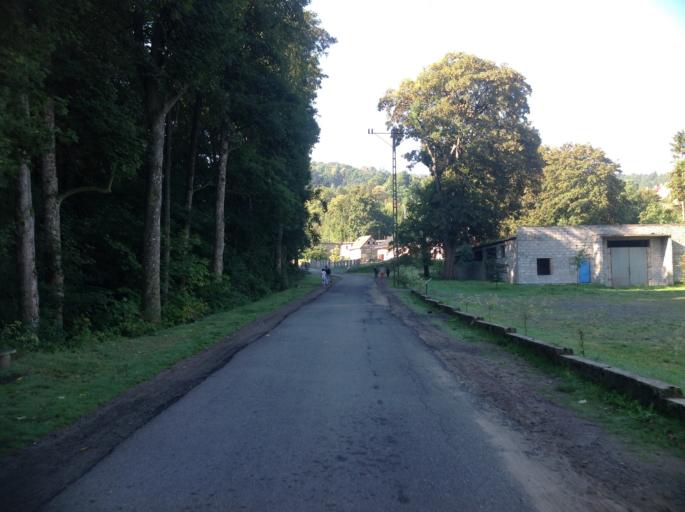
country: PL
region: Lower Silesian Voivodeship
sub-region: Powiat zabkowicki
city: Zloty Stok
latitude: 50.4432
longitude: 16.8781
